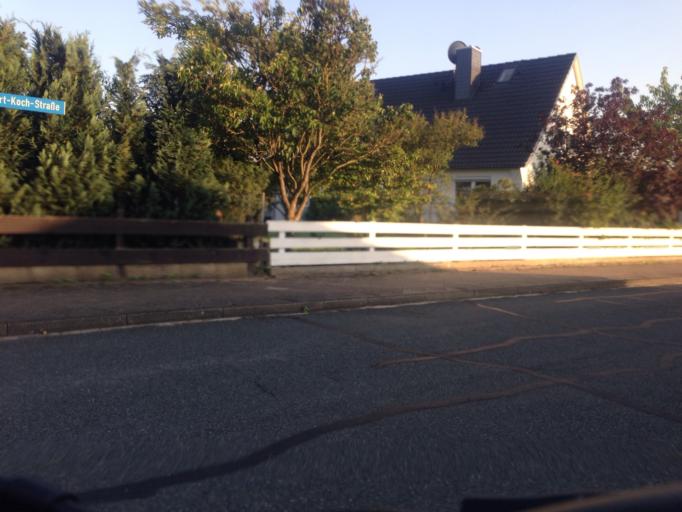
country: DE
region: Lower Saxony
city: Adendorf
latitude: 53.2825
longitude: 10.4511
